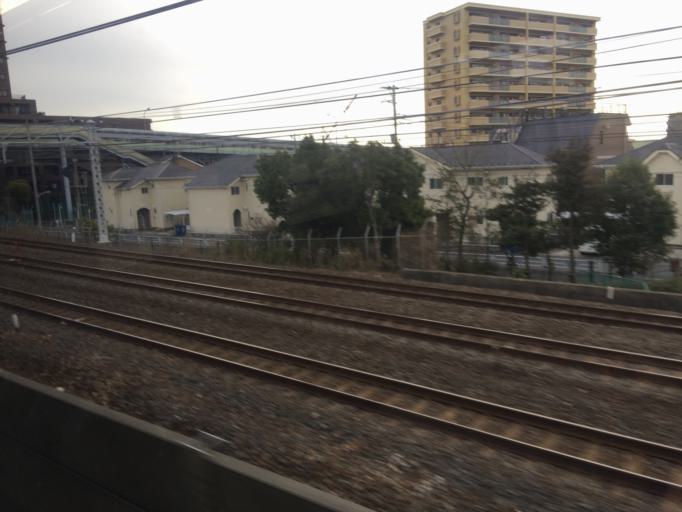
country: JP
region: Tokyo
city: Urayasu
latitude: 35.7256
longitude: 139.8704
